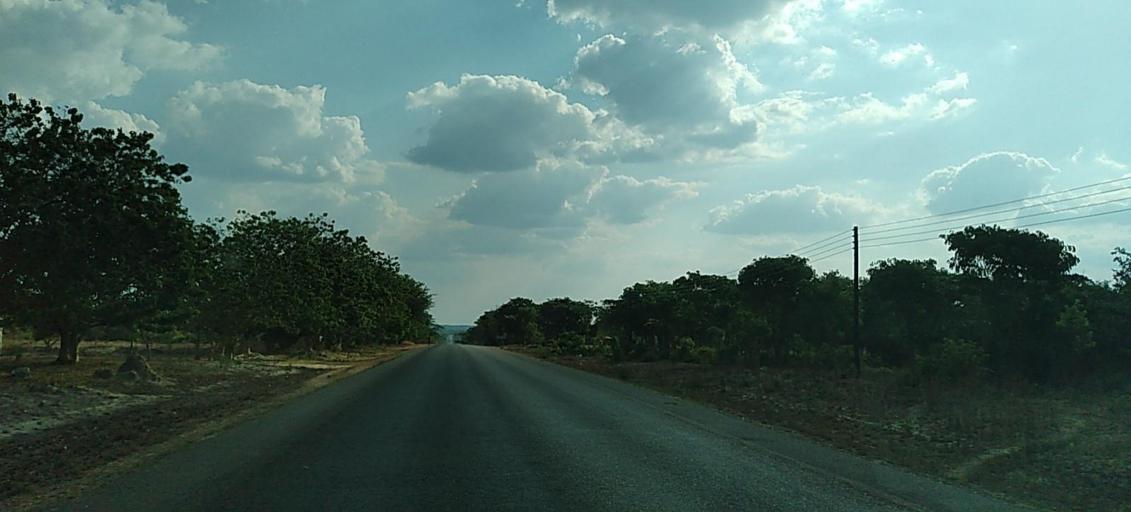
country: ZM
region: Copperbelt
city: Luanshya
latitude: -13.3681
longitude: 28.4045
